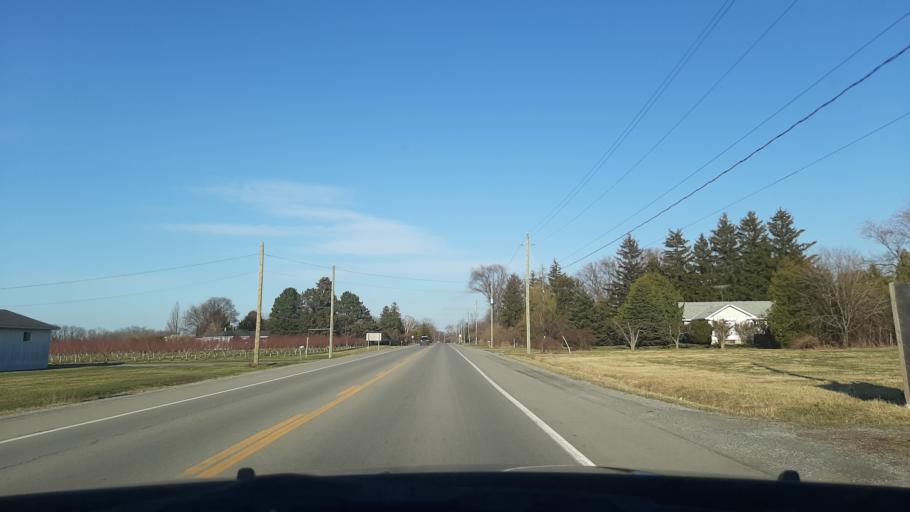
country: CA
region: Ontario
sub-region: Regional Municipality of Niagara
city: St. Catharines
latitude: 43.2229
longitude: -79.1886
